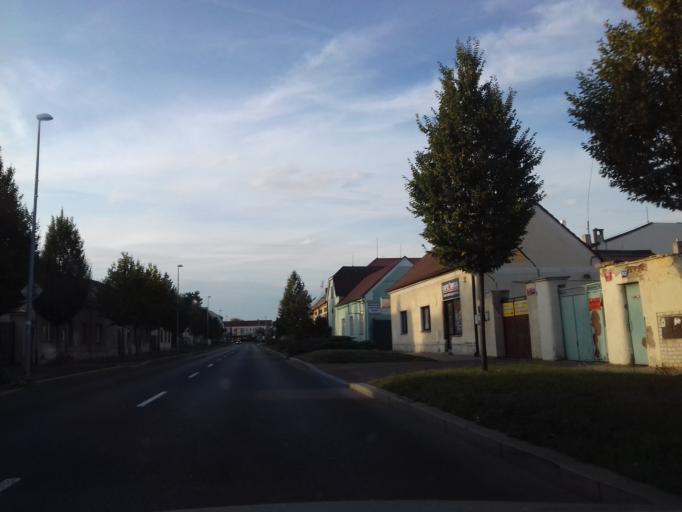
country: CZ
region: Praha
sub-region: Praha 4
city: Hodkovicky
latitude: 50.0117
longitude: 14.4590
